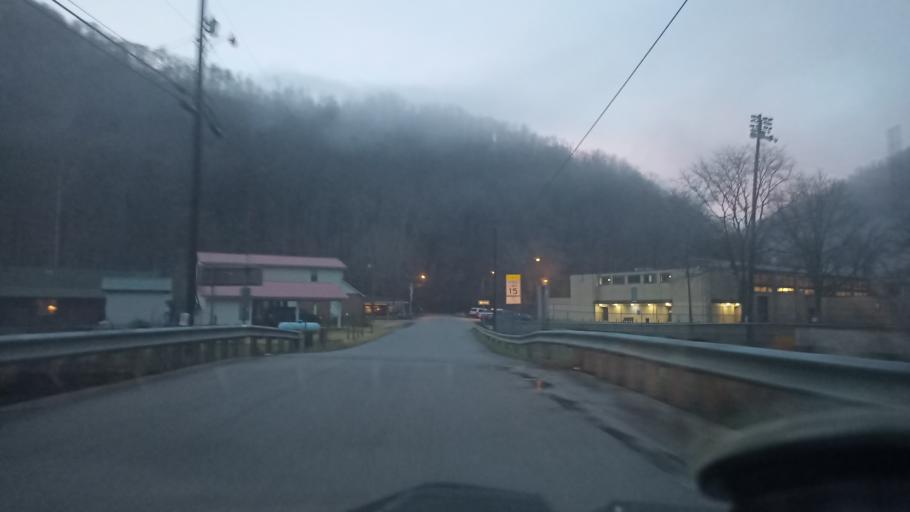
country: US
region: West Virginia
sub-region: Logan County
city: Mallory
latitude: 37.7293
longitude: -81.8776
